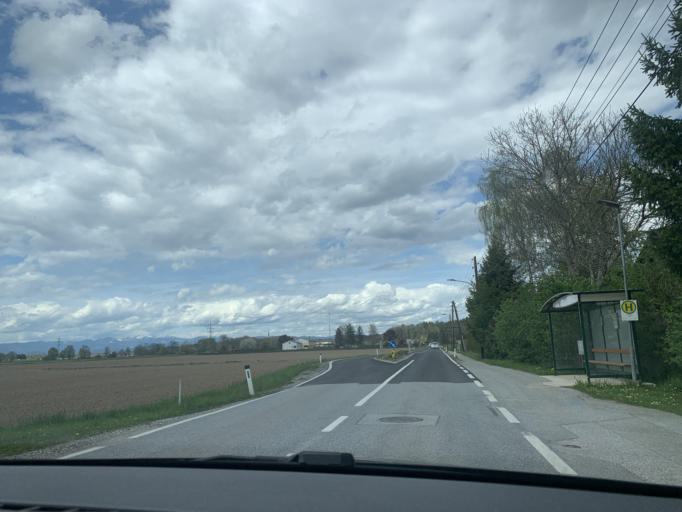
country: AT
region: Styria
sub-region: Politischer Bezirk Graz-Umgebung
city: Zettling
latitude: 46.9313
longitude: 15.3892
